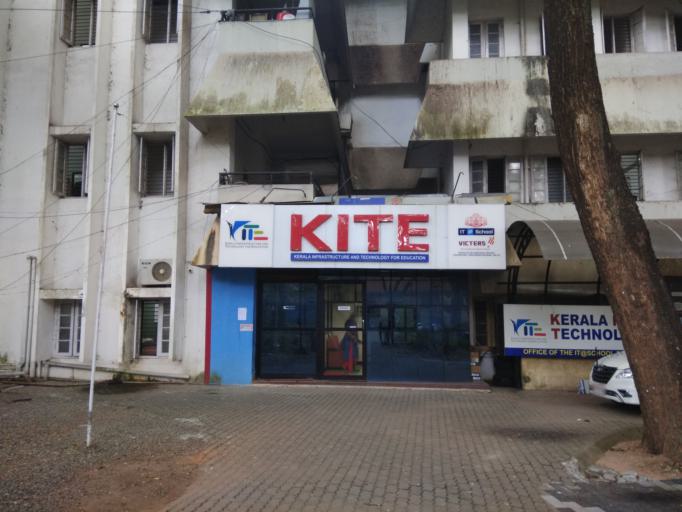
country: IN
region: Kerala
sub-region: Thiruvananthapuram
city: Thiruvananthapuram
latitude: 8.4897
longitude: 76.9726
